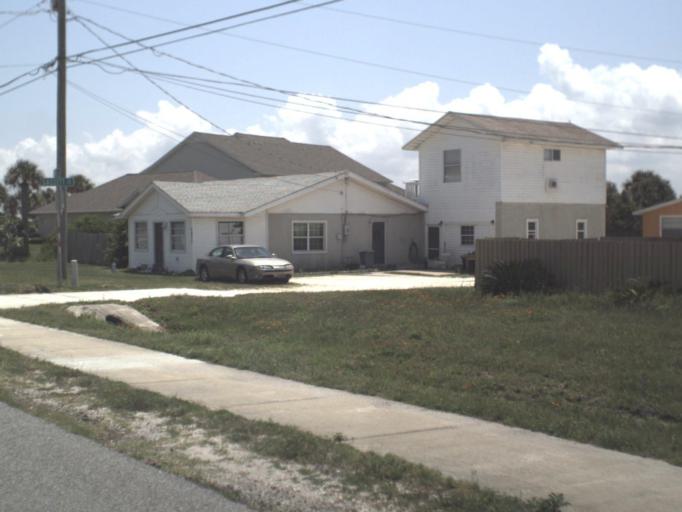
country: US
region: Florida
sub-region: Saint Johns County
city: Butler Beach
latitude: 29.7622
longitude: -81.2510
